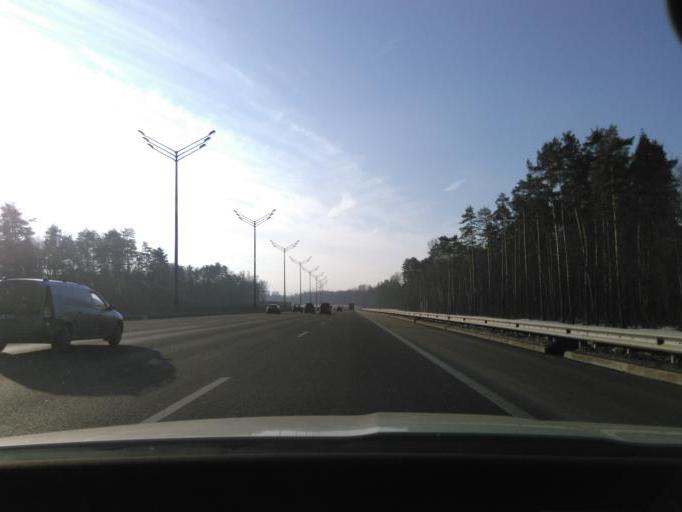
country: RU
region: Moscow
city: Khimki
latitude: 55.9246
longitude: 37.4543
